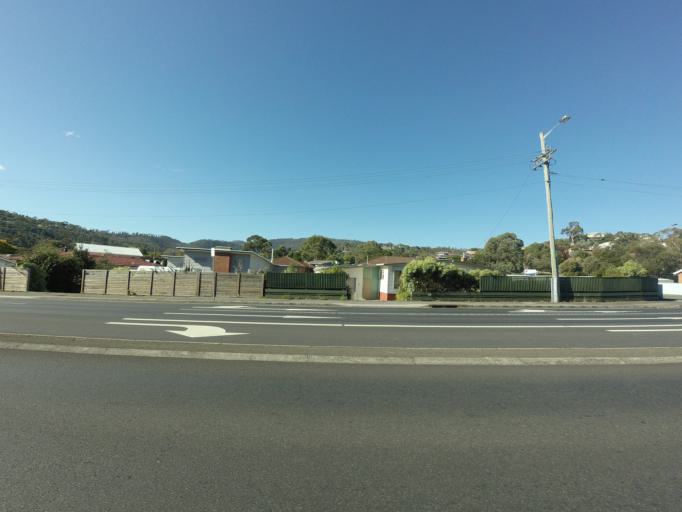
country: AU
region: Tasmania
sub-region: Clarence
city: Lindisfarne
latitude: -42.8389
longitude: 147.3516
